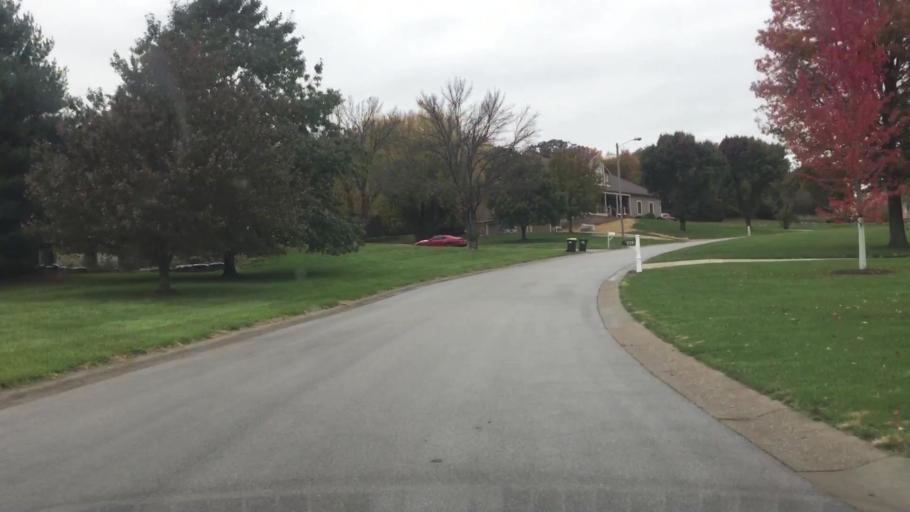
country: US
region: Kansas
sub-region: Wyandotte County
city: Edwardsville
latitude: 38.9937
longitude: -94.8243
